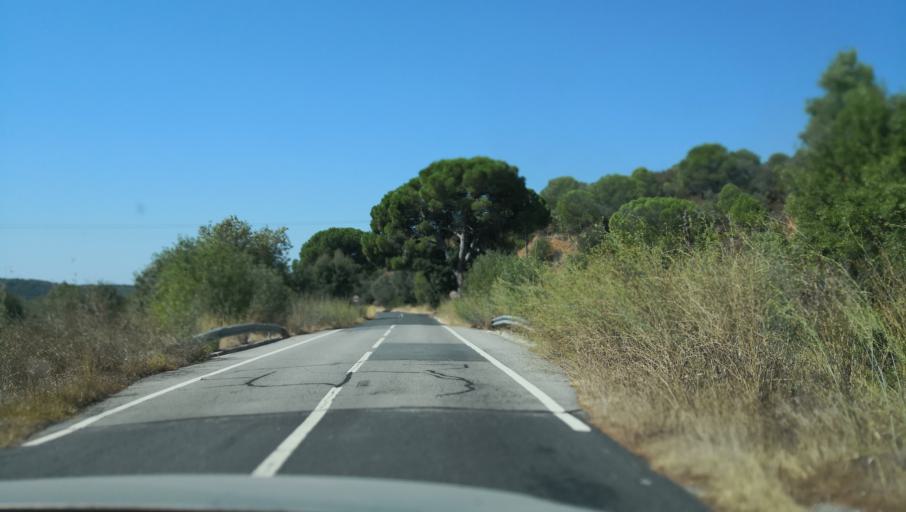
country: PT
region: Setubal
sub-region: Alcacer do Sal
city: Alcacer do Sal
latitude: 38.2792
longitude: -8.3852
